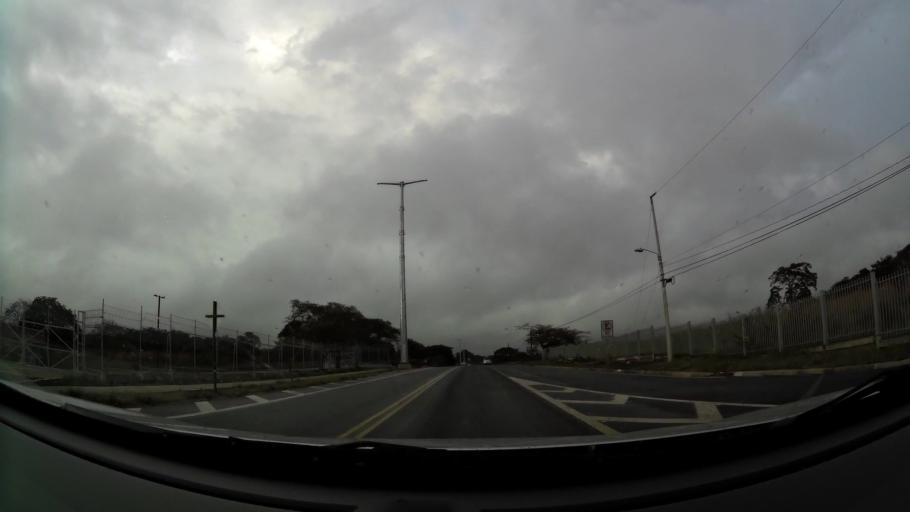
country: CR
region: Alajuela
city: Carrillos
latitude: 9.9755
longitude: -84.2752
